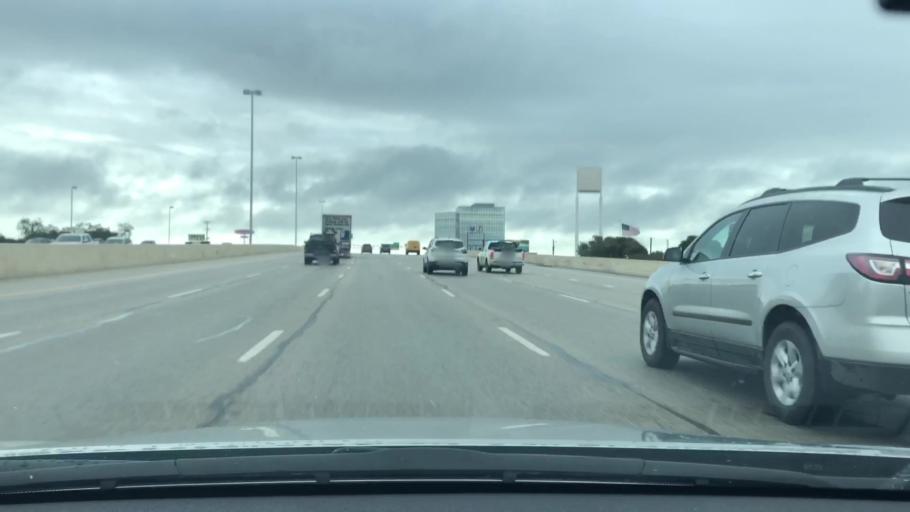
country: US
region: Texas
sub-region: Bexar County
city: Alamo Heights
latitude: 29.5160
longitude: -98.4545
